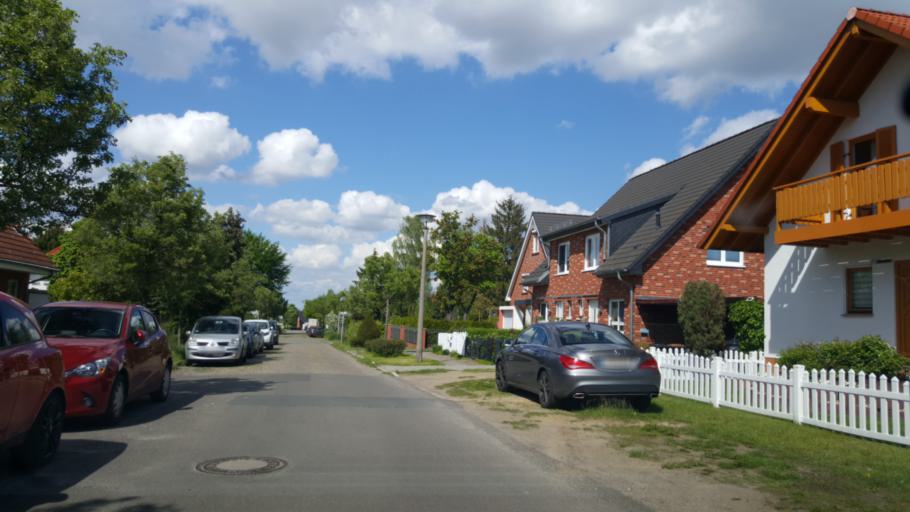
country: DE
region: Berlin
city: Altglienicke
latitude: 52.4156
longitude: 13.5445
